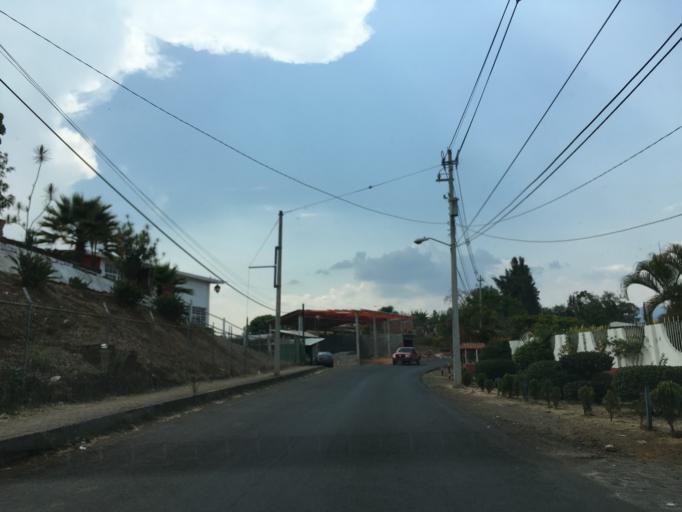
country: MX
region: Michoacan
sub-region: Ziracuaretiro
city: Patuan
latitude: 19.4172
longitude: -101.9185
